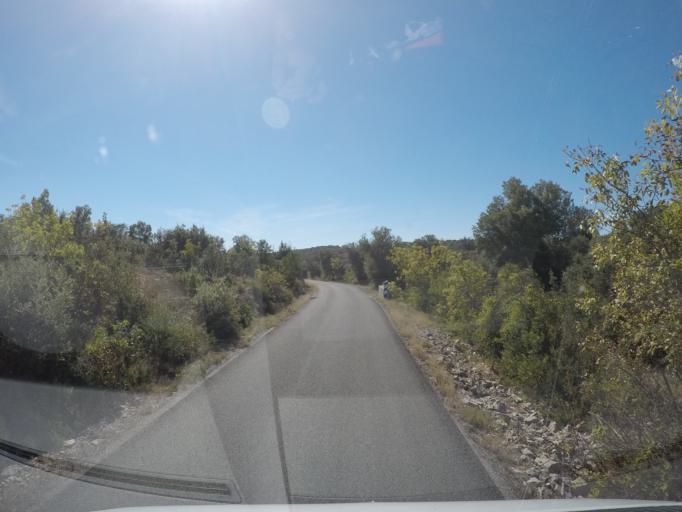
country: FR
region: Languedoc-Roussillon
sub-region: Departement de l'Herault
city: Vailhauques
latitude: 43.7265
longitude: 3.6758
